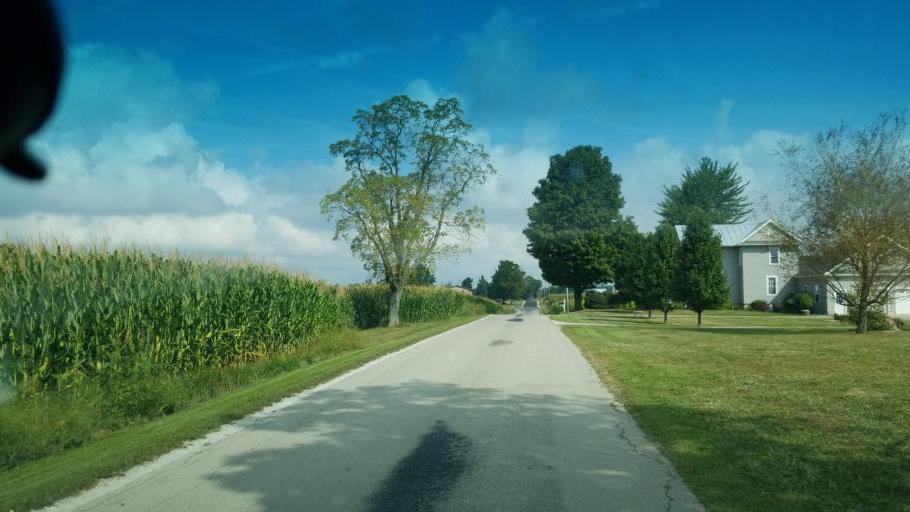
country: US
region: Ohio
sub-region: Hardin County
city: Forest
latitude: 40.8591
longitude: -83.5059
